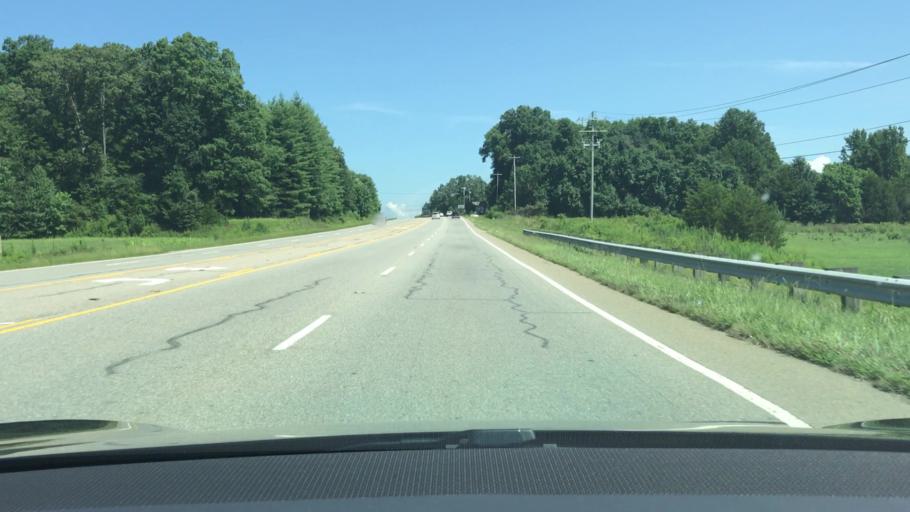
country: US
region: North Carolina
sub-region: Macon County
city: Franklin
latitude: 35.1010
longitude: -83.3853
